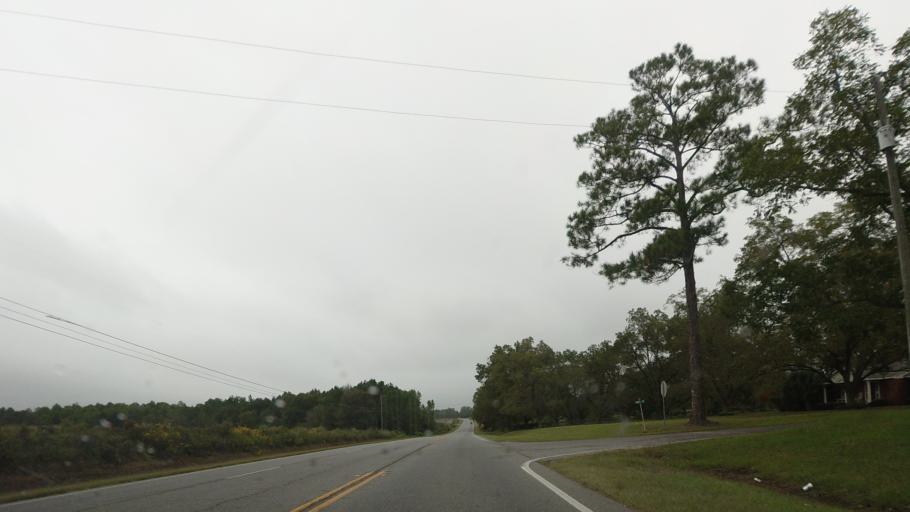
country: US
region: Georgia
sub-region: Ben Hill County
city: Fitzgerald
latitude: 31.6752
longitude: -83.2361
